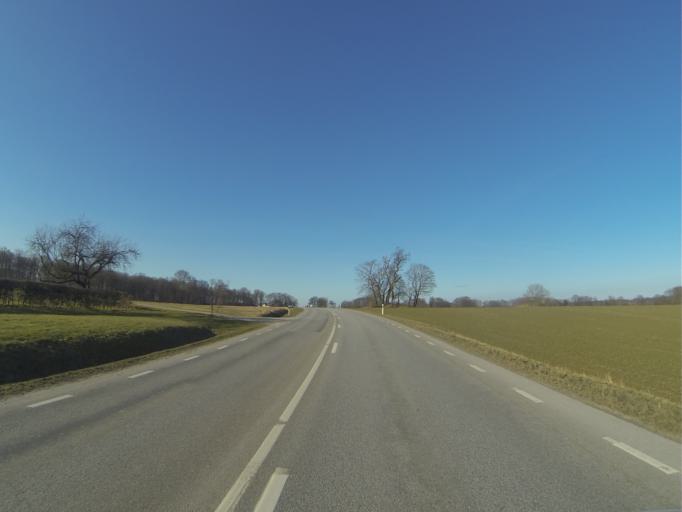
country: SE
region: Skane
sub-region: Hoors Kommun
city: Satofta
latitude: 55.8614
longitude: 13.4994
